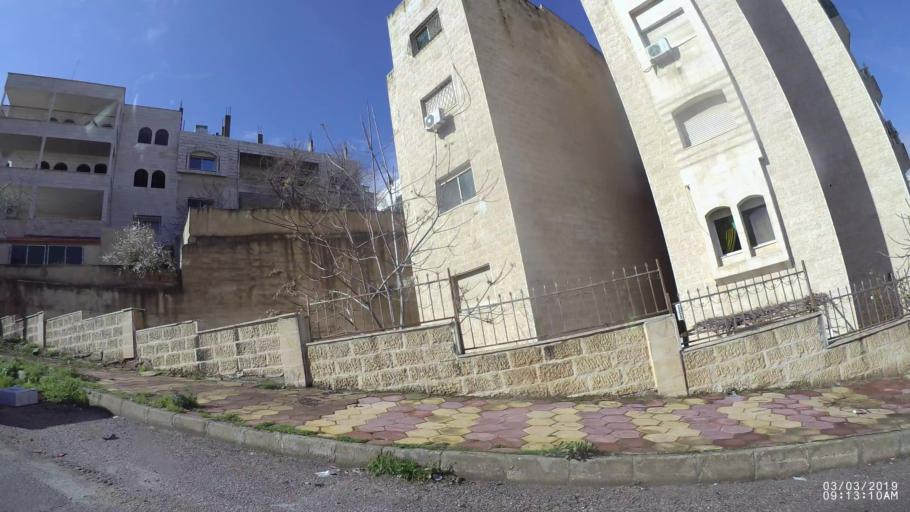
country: JO
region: Amman
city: Al Jubayhah
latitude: 32.0022
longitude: 35.8930
